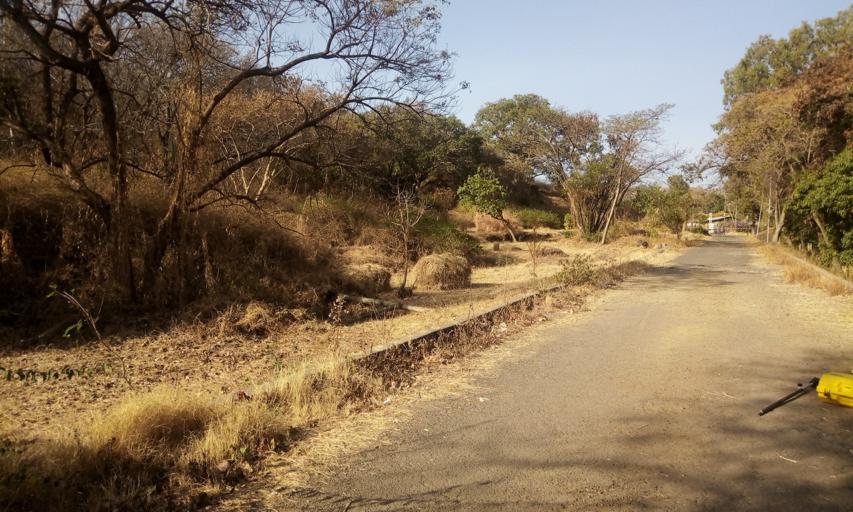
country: ET
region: Amhara
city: Gondar
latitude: 12.2382
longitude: 37.3011
